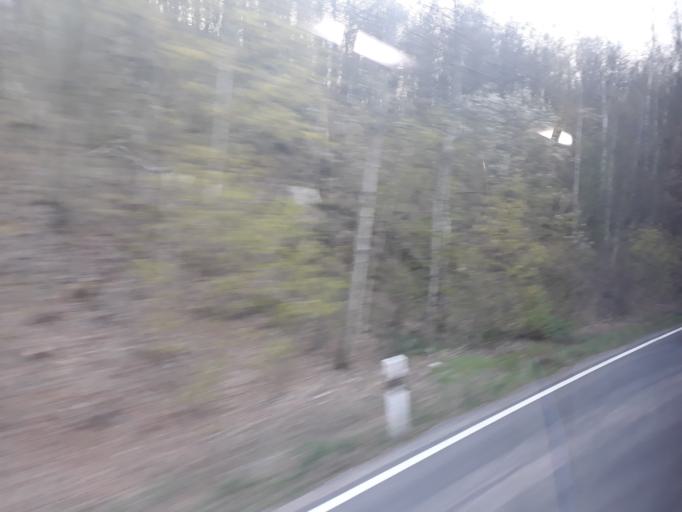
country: DE
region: Saxony
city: Kreischa
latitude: 50.9606
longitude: 13.7782
